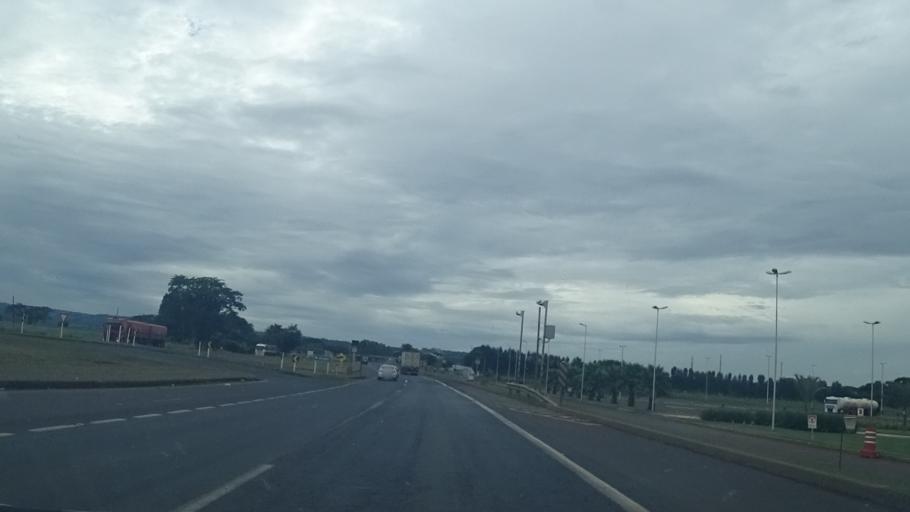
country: BR
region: Minas Gerais
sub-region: Centralina
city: Centralina
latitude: -18.5750
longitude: -49.1939
